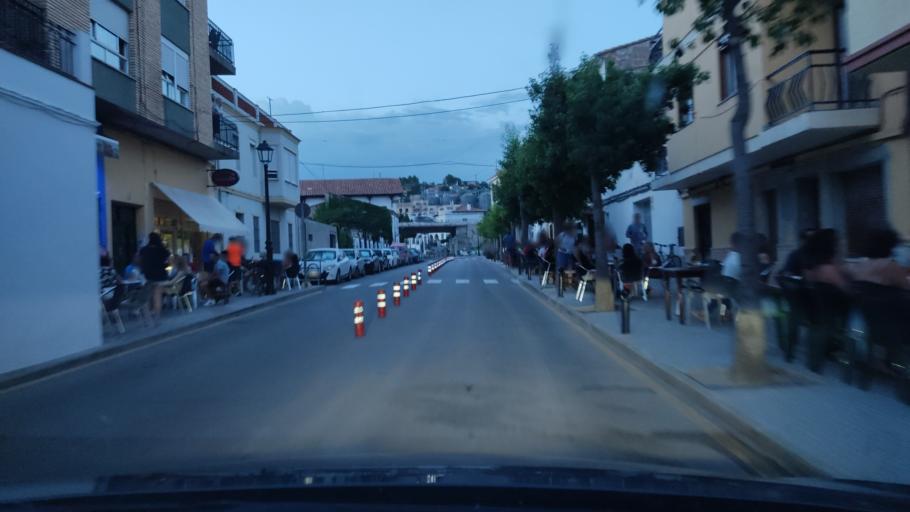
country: ES
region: Valencia
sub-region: Provincia de Castello
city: Jerica
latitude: 39.9132
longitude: -0.5719
